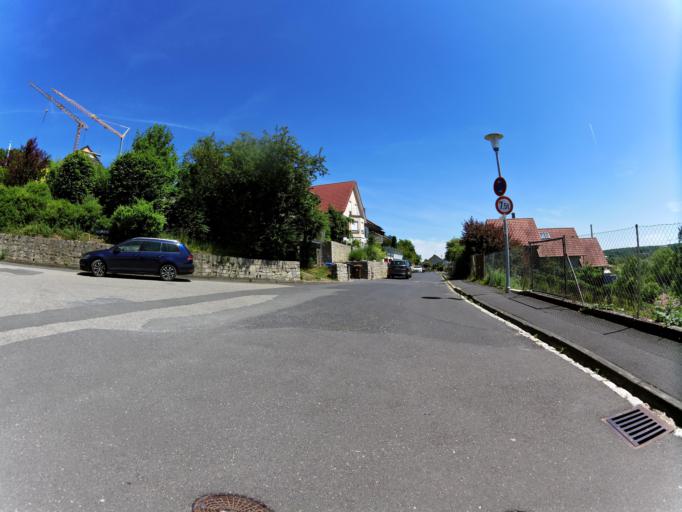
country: DE
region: Bavaria
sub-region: Regierungsbezirk Unterfranken
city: Ochsenfurt
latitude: 49.6697
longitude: 10.0692
